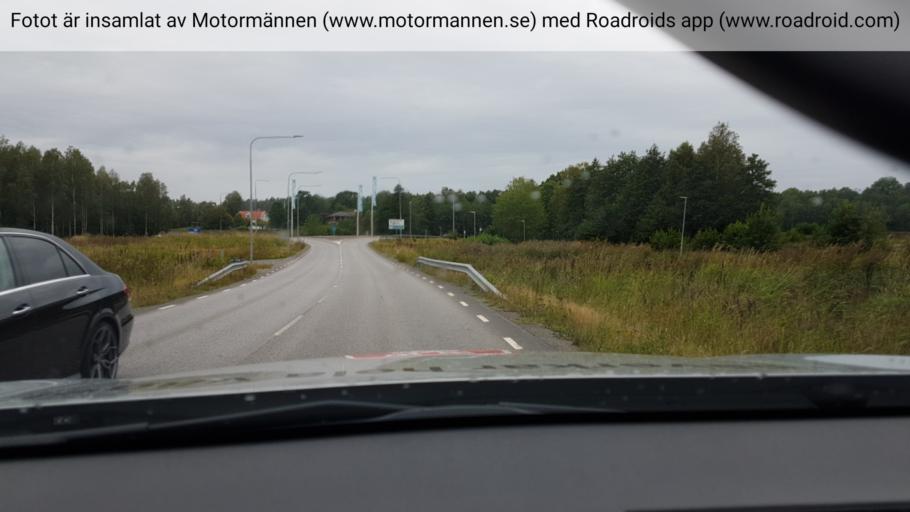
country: SE
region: Vaestra Goetaland
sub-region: Trollhattan
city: Trollhattan
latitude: 58.3133
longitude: 12.2987
